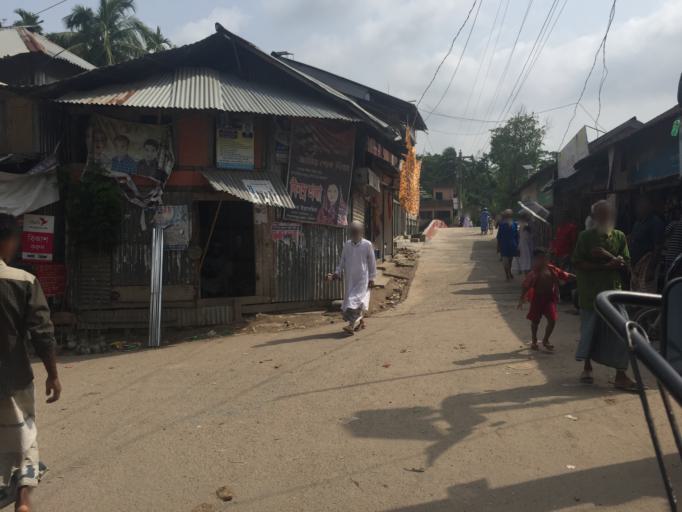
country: BD
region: Barisal
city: Mathba
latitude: 22.2448
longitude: 89.9144
